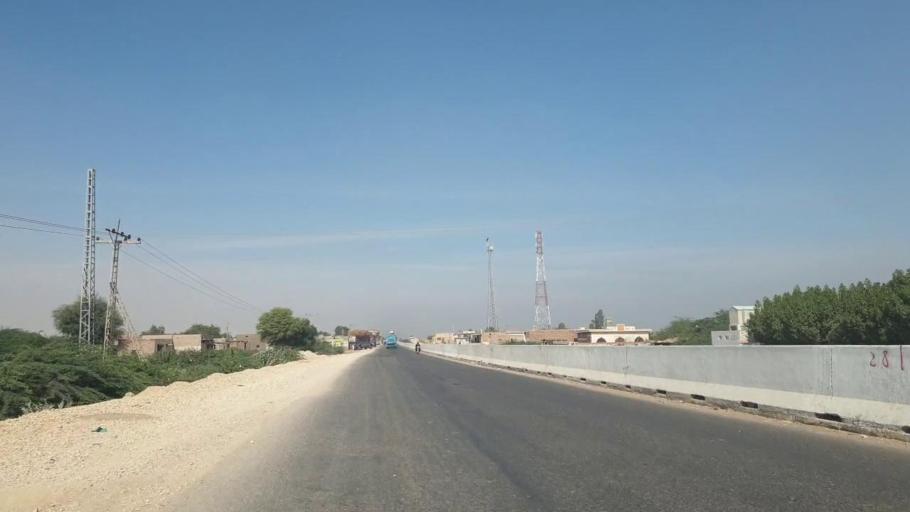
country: PK
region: Sindh
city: Matiari
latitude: 25.6473
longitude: 68.3010
